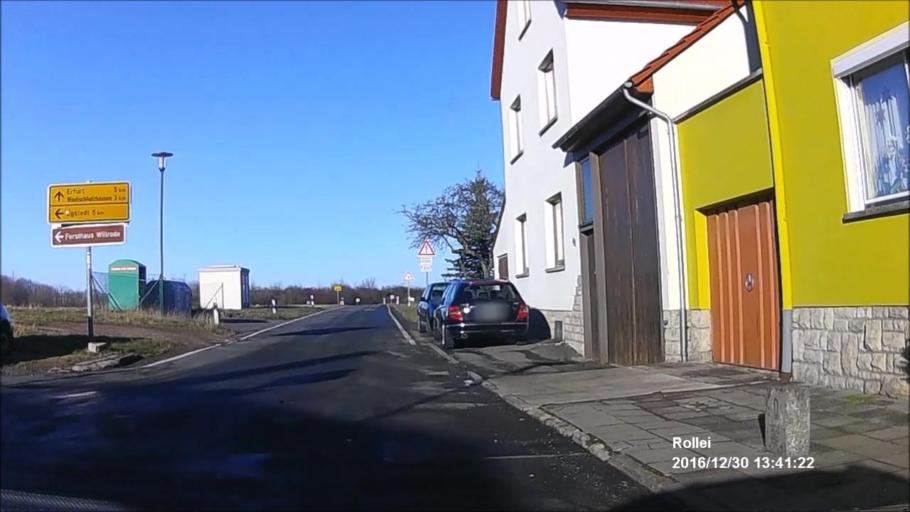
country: DE
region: Thuringia
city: Klettbach
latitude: 50.9176
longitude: 11.1147
